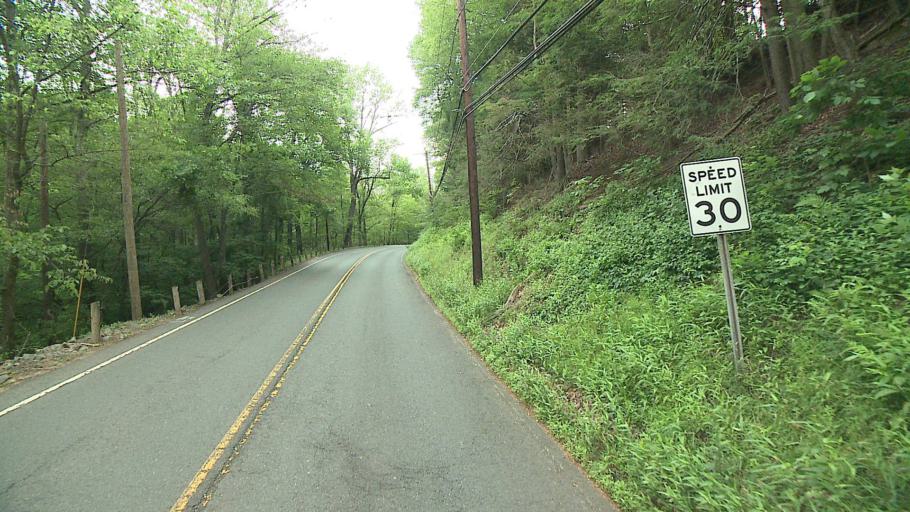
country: US
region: Connecticut
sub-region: Hartford County
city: Collinsville
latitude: 41.8186
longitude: -72.9165
